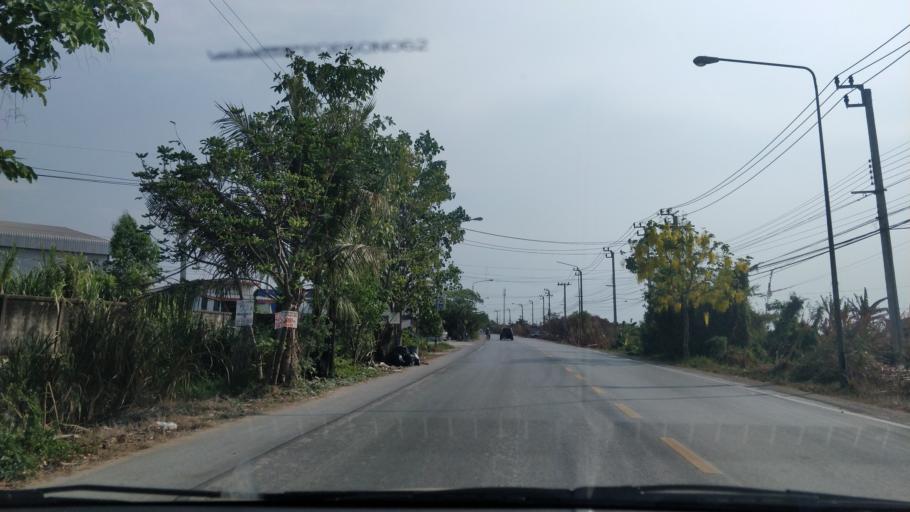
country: TH
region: Bangkok
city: Saphan Sung
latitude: 13.7527
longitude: 100.7192
